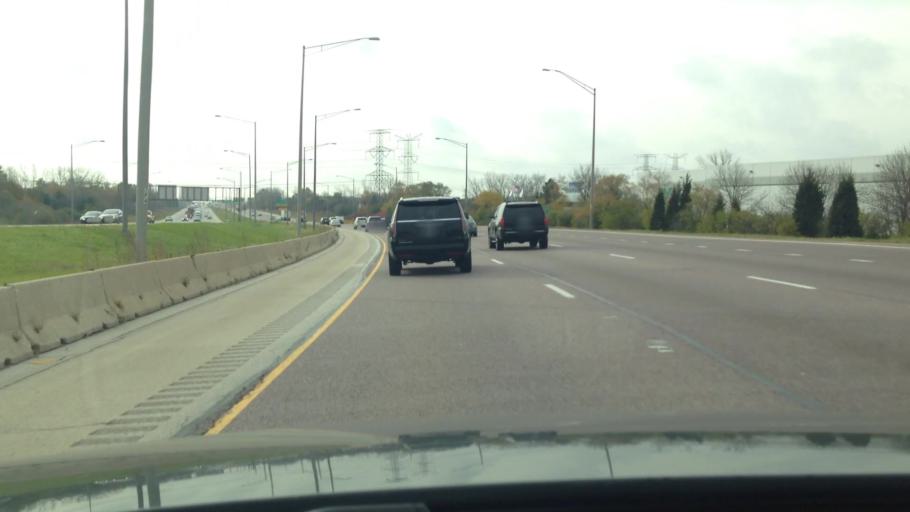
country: US
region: Illinois
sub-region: DuPage County
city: Itasca
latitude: 41.9481
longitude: -88.0374
